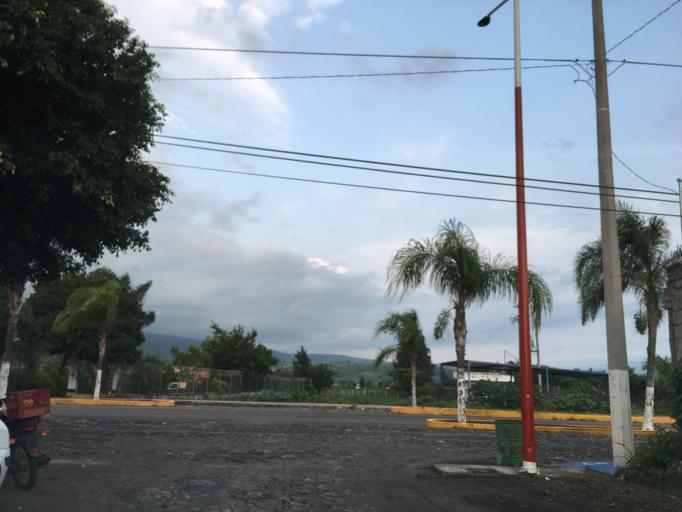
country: MX
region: Nayarit
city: Jala
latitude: 21.0976
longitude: -104.4341
